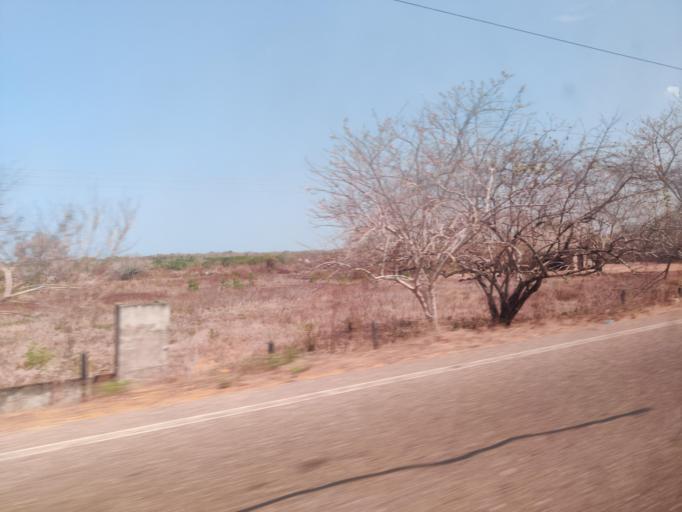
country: CO
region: Bolivar
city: Turbana
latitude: 10.2156
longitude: -75.5933
